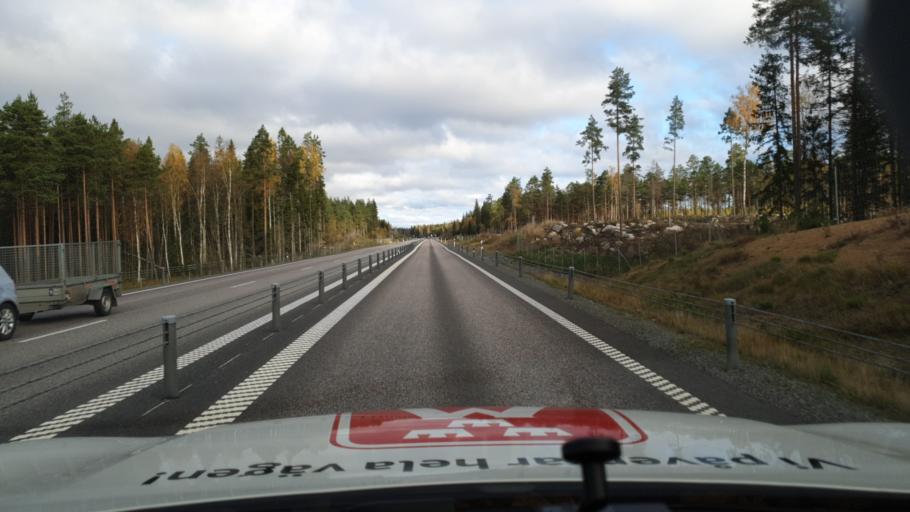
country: SE
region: Uppsala
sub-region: Heby Kommun
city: Tarnsjo
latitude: 60.1093
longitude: 16.9220
